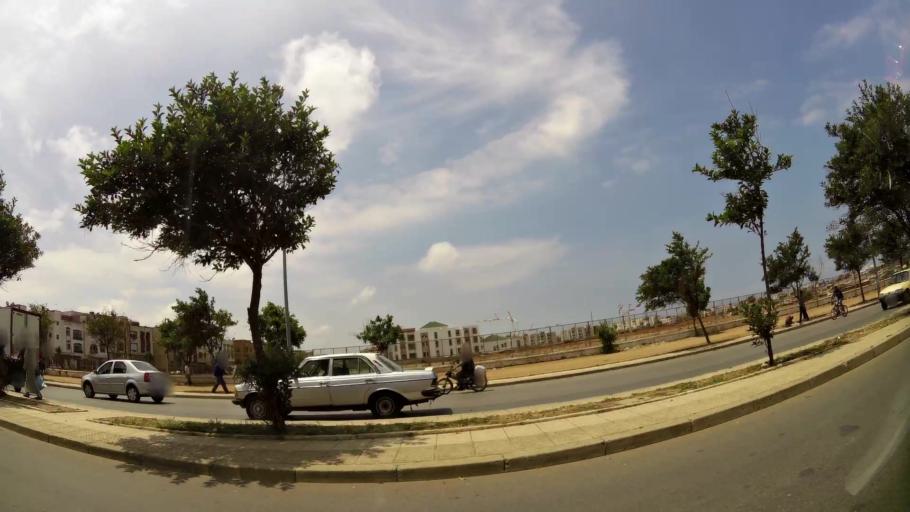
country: MA
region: Rabat-Sale-Zemmour-Zaer
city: Sale
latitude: 34.0490
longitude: -6.7875
